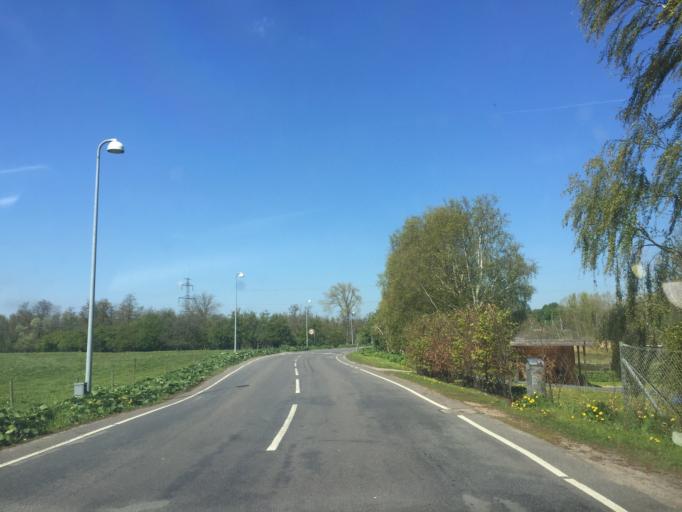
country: DK
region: Capital Region
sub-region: Hoje-Taastrup Kommune
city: Taastrup
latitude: 55.6842
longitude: 12.2483
